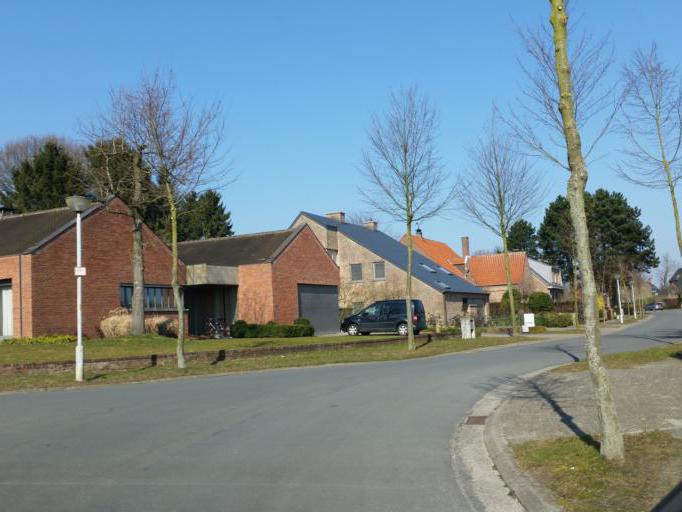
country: BE
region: Flanders
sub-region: Provincie Oost-Vlaanderen
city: Kruibeke
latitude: 51.1481
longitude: 4.3042
